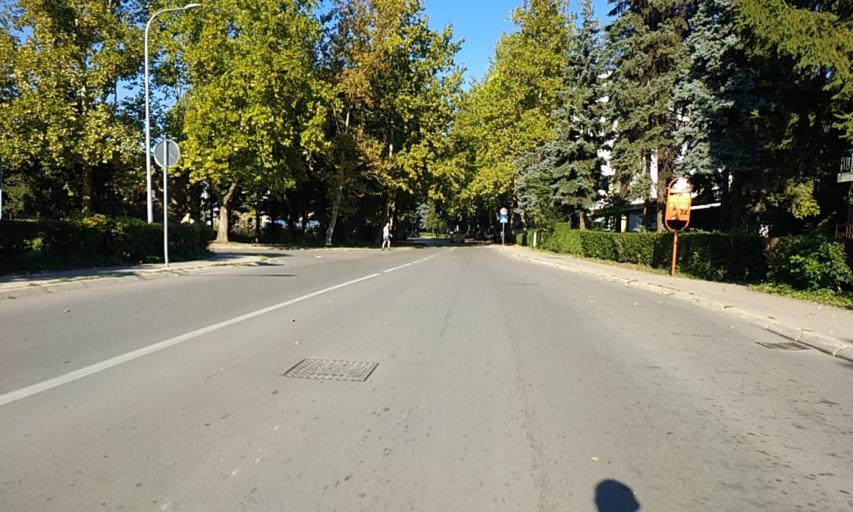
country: BA
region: Republika Srpska
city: Starcevica
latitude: 44.7632
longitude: 17.2102
